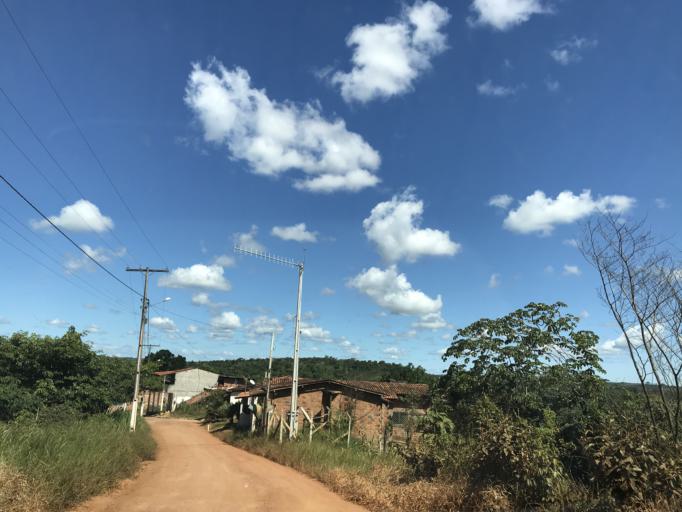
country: BR
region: Bahia
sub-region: Valenca
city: Valenca
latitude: -13.3220
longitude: -39.2412
